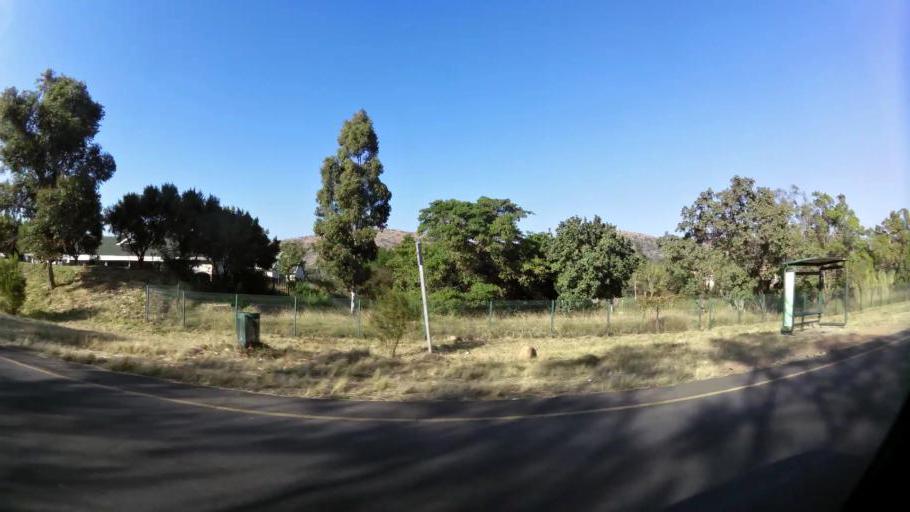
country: ZA
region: Gauteng
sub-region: City of Tshwane Metropolitan Municipality
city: Pretoria
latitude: -25.6776
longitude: 28.1400
